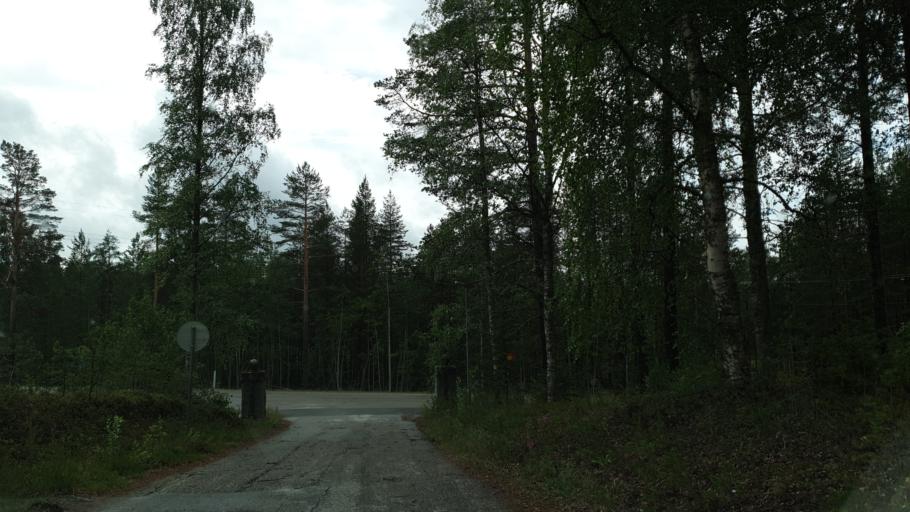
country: FI
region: Kainuu
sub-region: Kehys-Kainuu
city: Kuhmo
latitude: 64.0937
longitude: 29.4338
